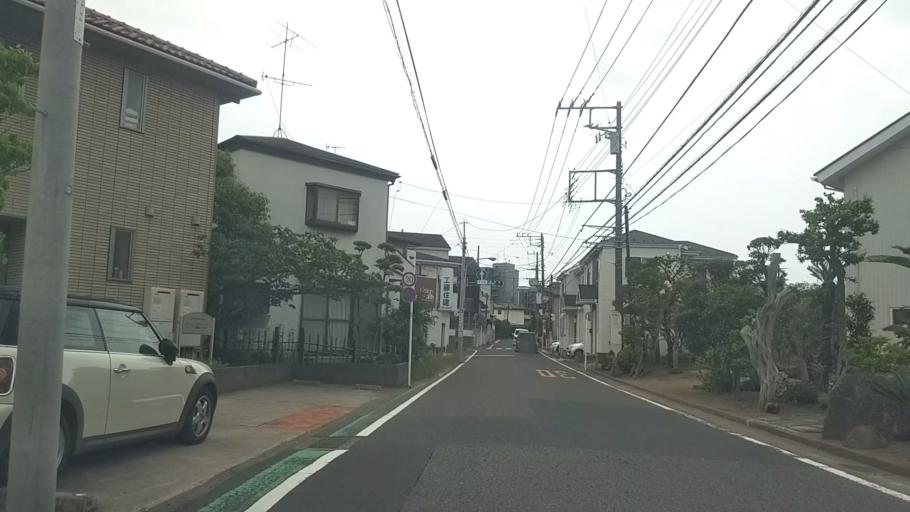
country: JP
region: Kanagawa
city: Fujisawa
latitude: 35.3449
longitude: 139.4555
